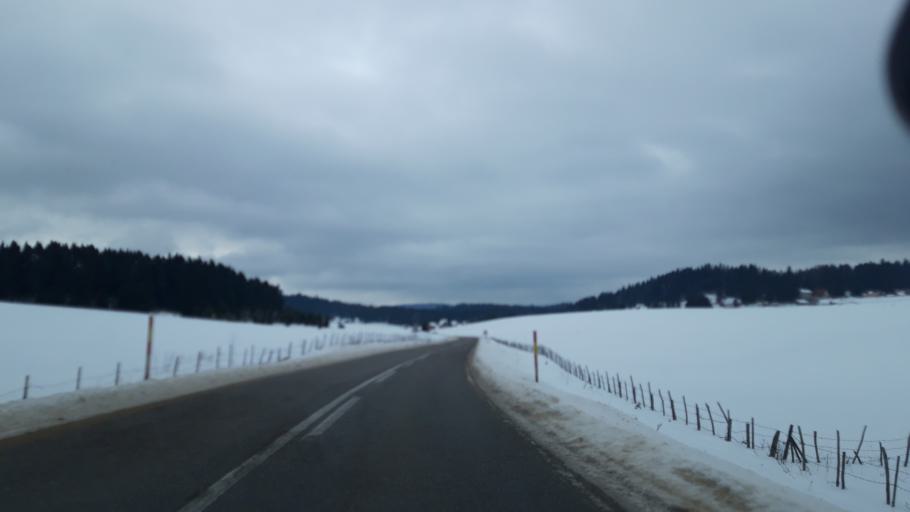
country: BA
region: Republika Srpska
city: Han Pijesak
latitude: 44.0991
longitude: 18.9651
